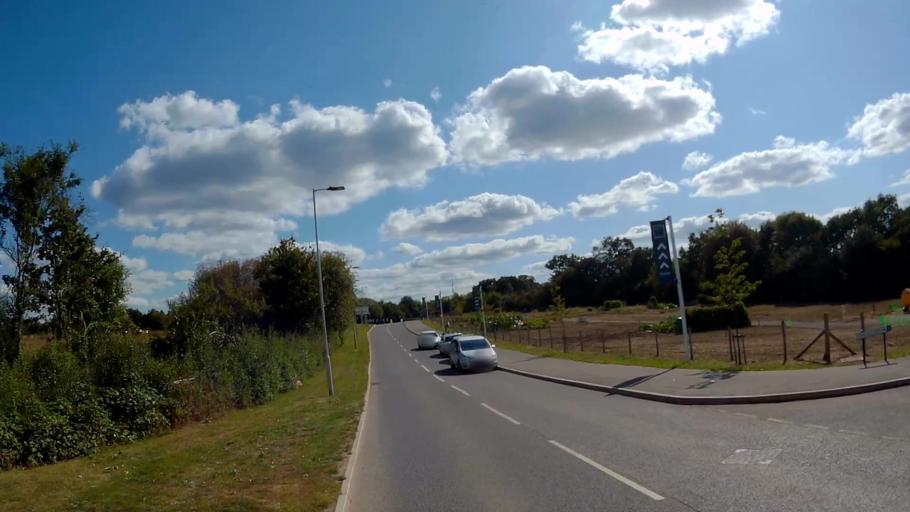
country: GB
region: England
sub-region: Bracknell Forest
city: Bracknell
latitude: 51.4311
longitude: -0.7509
